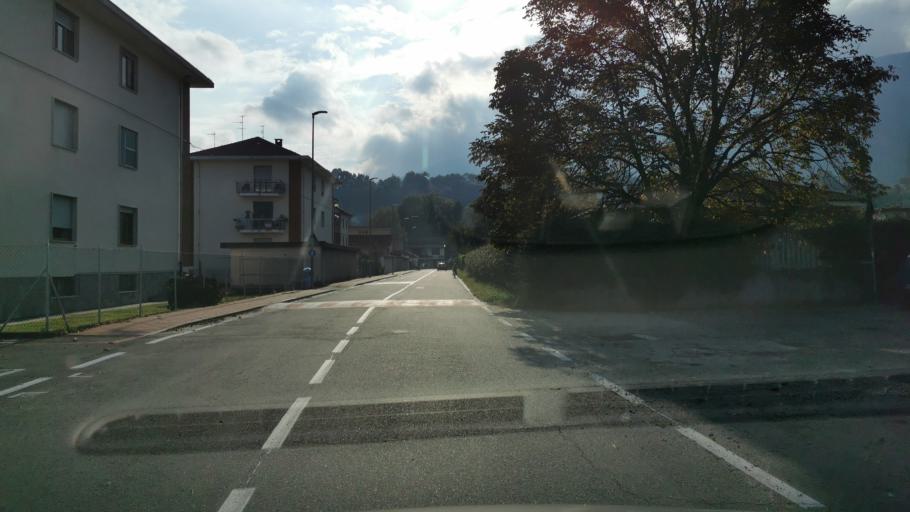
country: IT
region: Piedmont
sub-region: Provincia di Torino
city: Cafasse
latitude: 45.2440
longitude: 7.5206
